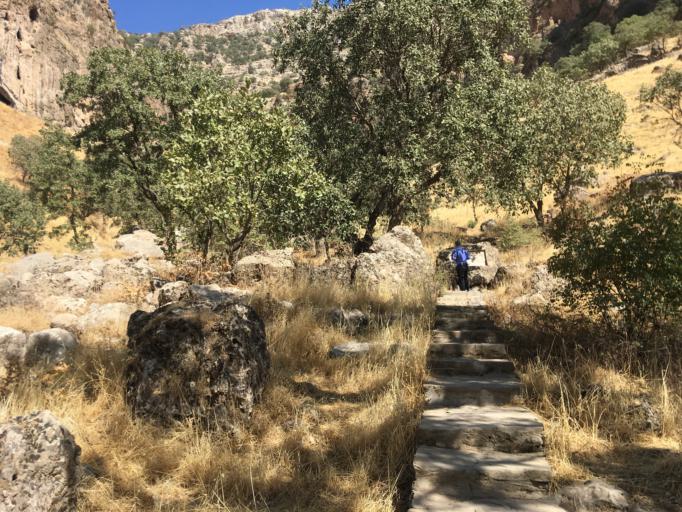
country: IQ
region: Arbil
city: Mergasur
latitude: 36.8334
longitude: 44.2186
